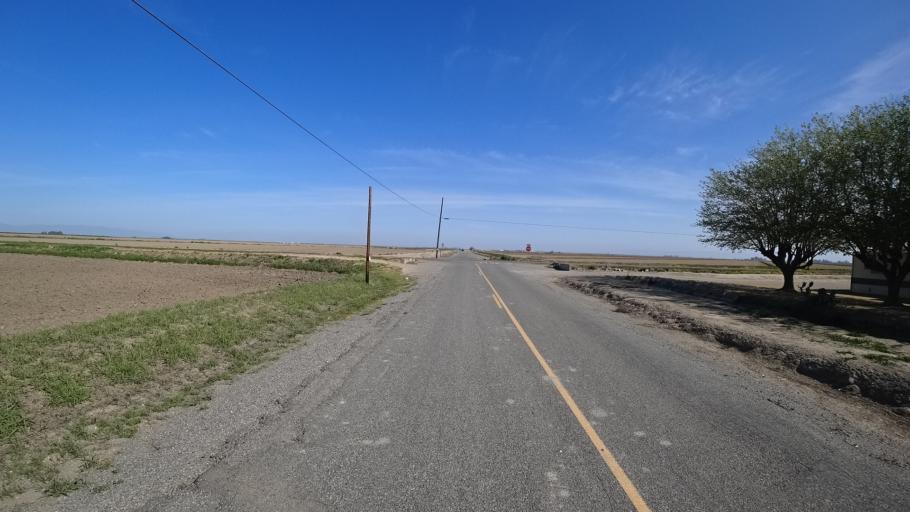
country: US
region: California
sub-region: Glenn County
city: Willows
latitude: 39.5817
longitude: -122.1170
